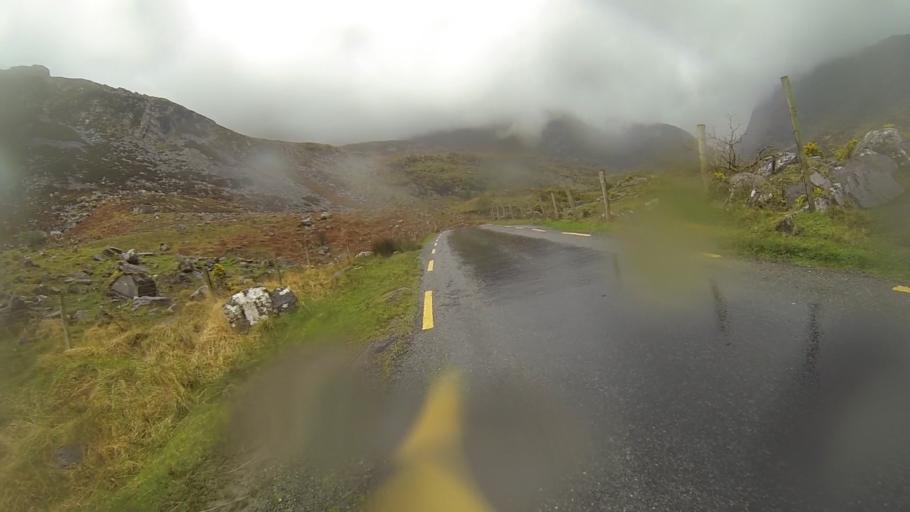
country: IE
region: Munster
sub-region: Ciarrai
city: Cill Airne
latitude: 52.0280
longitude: -9.6354
